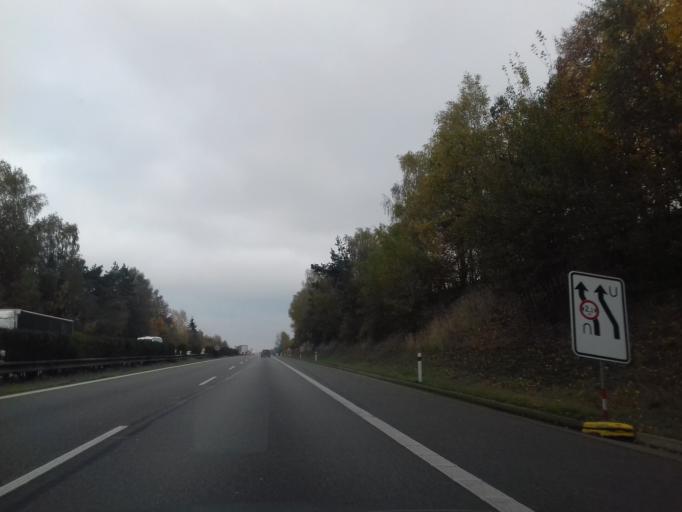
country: CZ
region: Central Bohemia
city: Trhovy Stepanov
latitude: 49.7199
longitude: 15.0513
